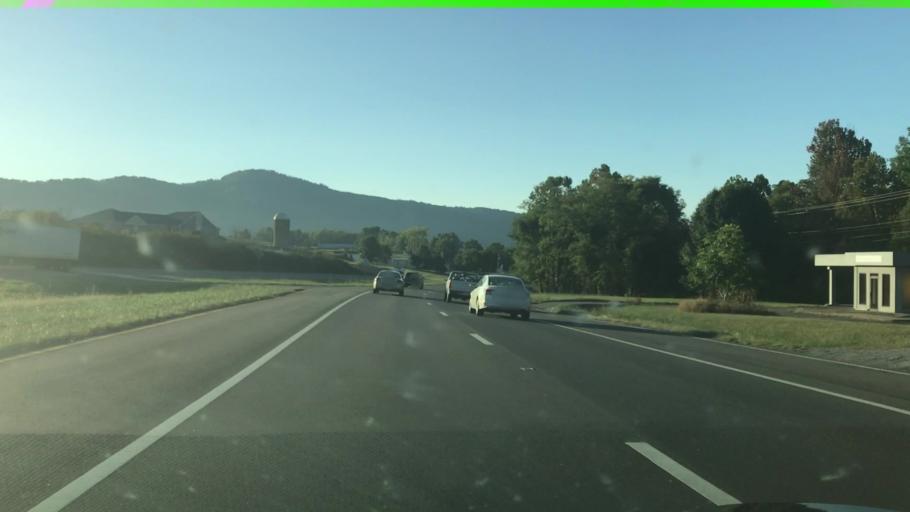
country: US
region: Virginia
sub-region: Botetourt County
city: Laymantown
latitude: 37.3410
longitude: -79.8766
